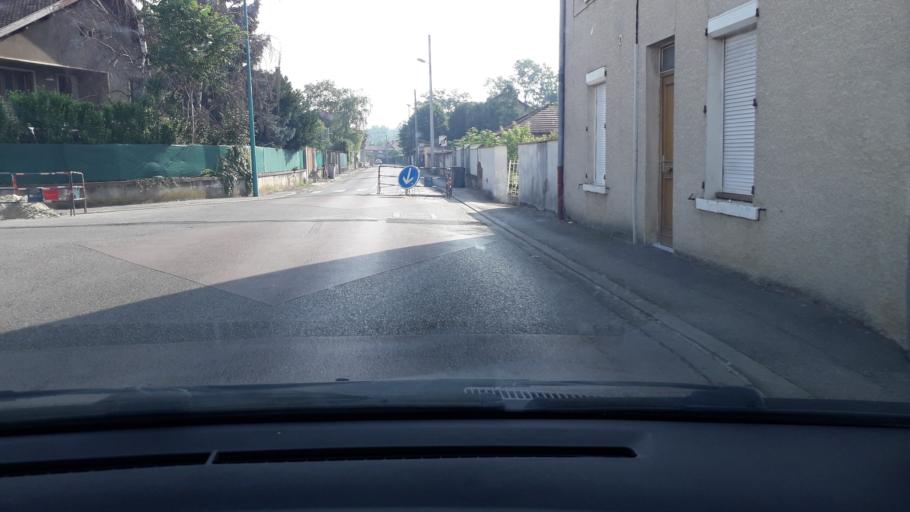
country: FR
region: Rhone-Alpes
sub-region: Departement de l'Isere
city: Pont-de-Cheruy
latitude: 45.7532
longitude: 5.1752
